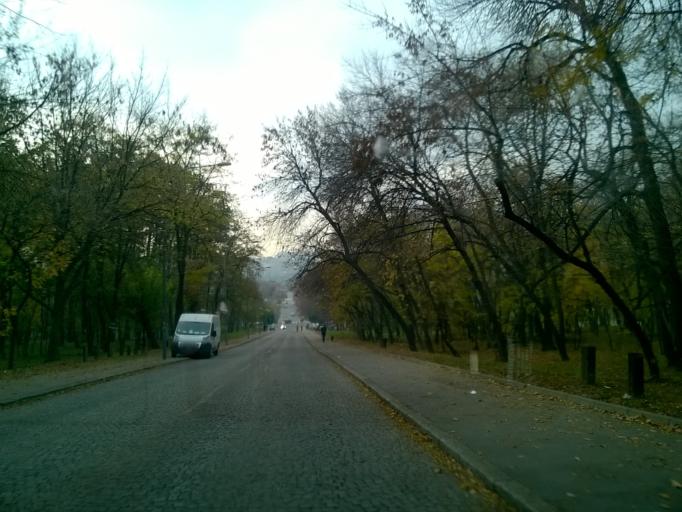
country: RS
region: Central Serbia
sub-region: Belgrade
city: Vozdovac
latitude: 44.7860
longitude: 20.4913
